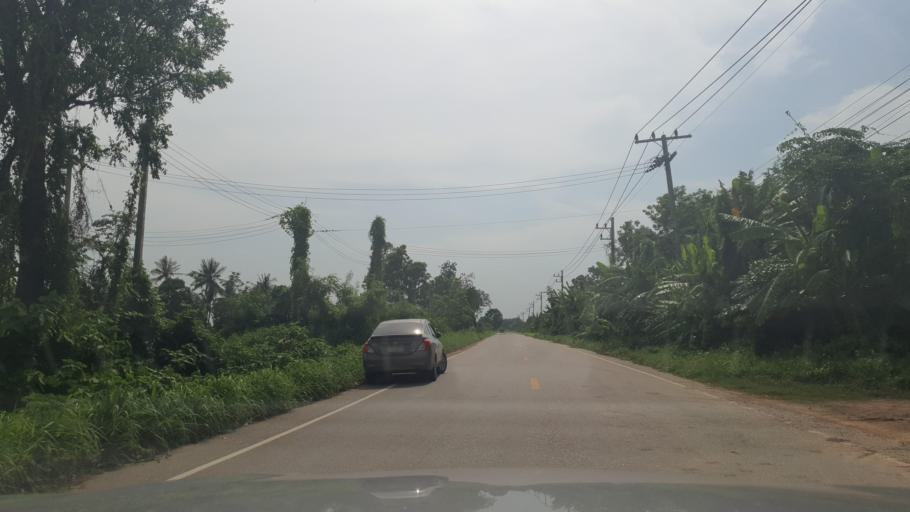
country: TH
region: Sukhothai
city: Si Samrong
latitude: 17.1156
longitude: 99.8859
